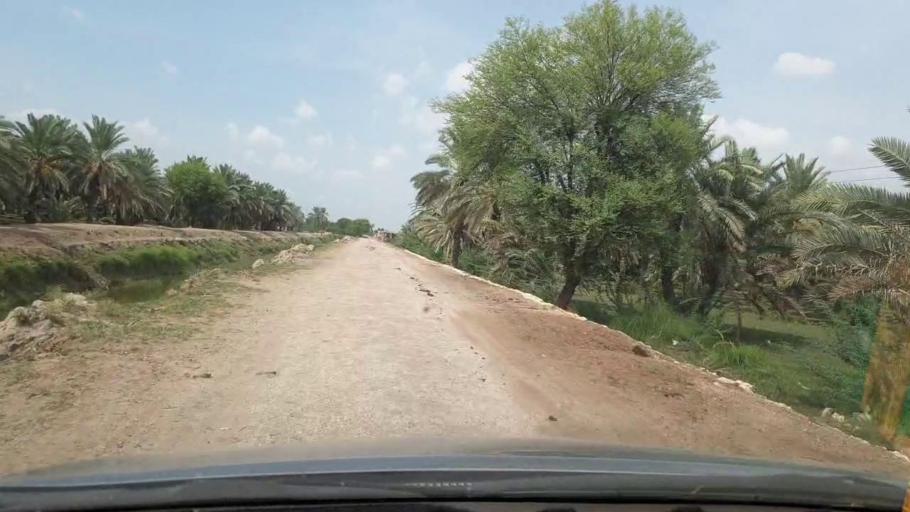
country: PK
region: Sindh
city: Khairpur
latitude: 27.5221
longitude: 68.8841
